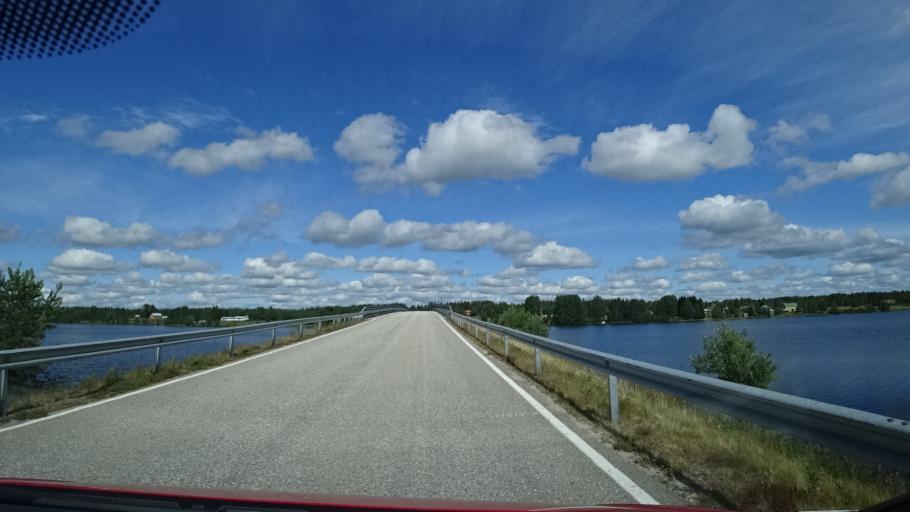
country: FI
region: Kainuu
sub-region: Kehys-Kainuu
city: Suomussalmi
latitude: 64.7399
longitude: 29.4391
